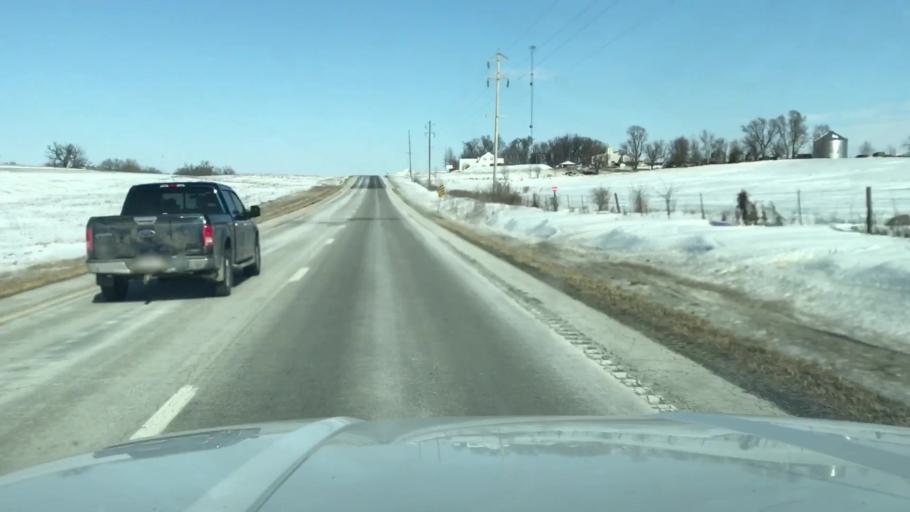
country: US
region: Missouri
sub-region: Nodaway County
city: Maryville
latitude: 40.1762
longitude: -94.8688
